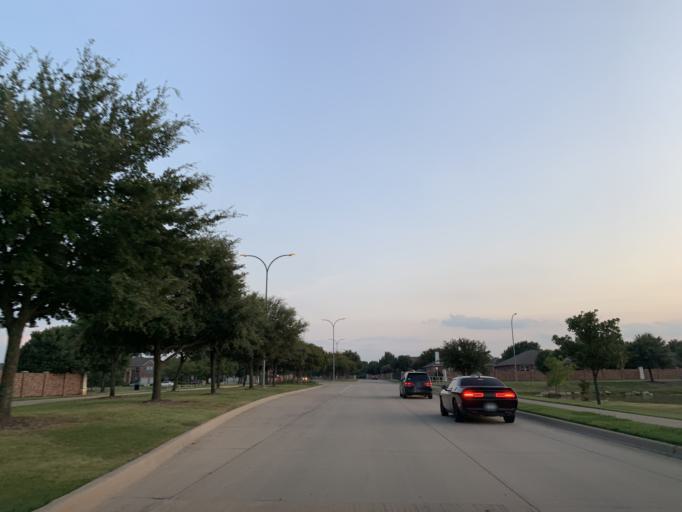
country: US
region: Texas
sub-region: Tarrant County
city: Keller
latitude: 32.9431
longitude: -97.2712
